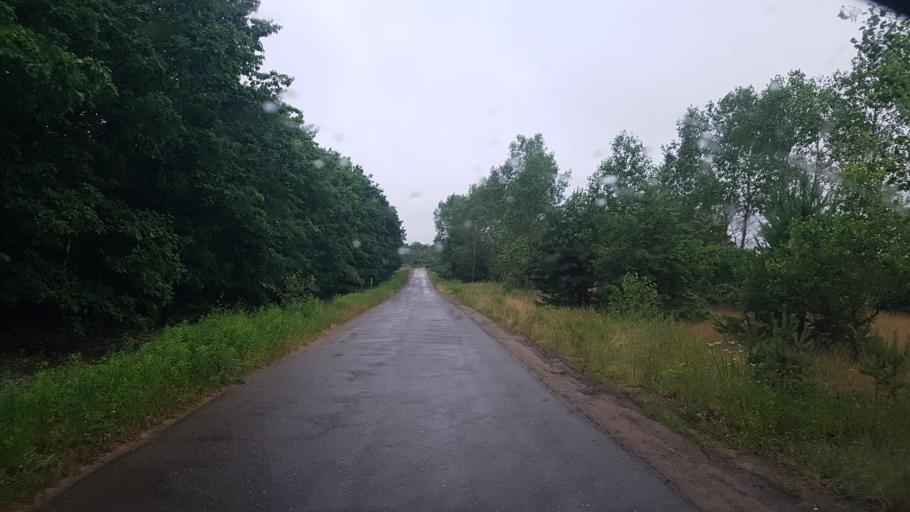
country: DE
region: Brandenburg
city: Lauchhammer
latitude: 51.5412
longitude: 13.7517
